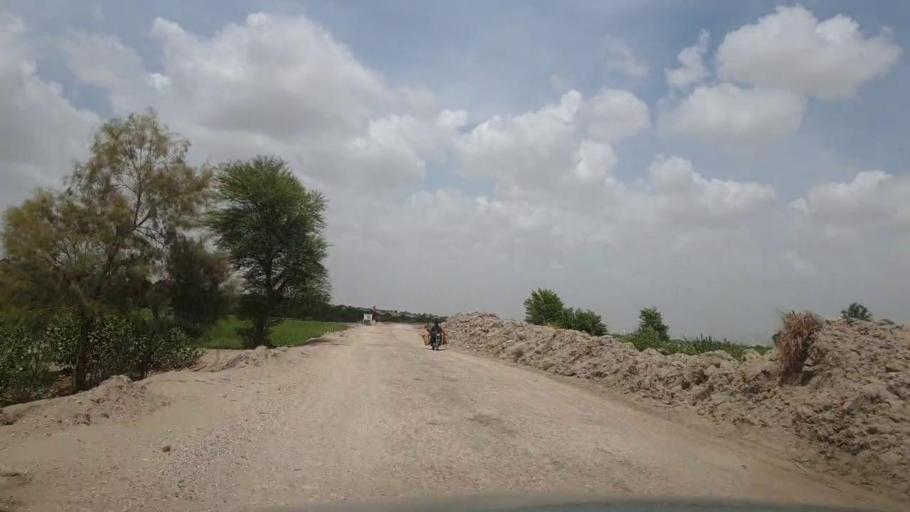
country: PK
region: Sindh
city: Kot Diji
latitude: 27.2161
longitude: 69.1002
